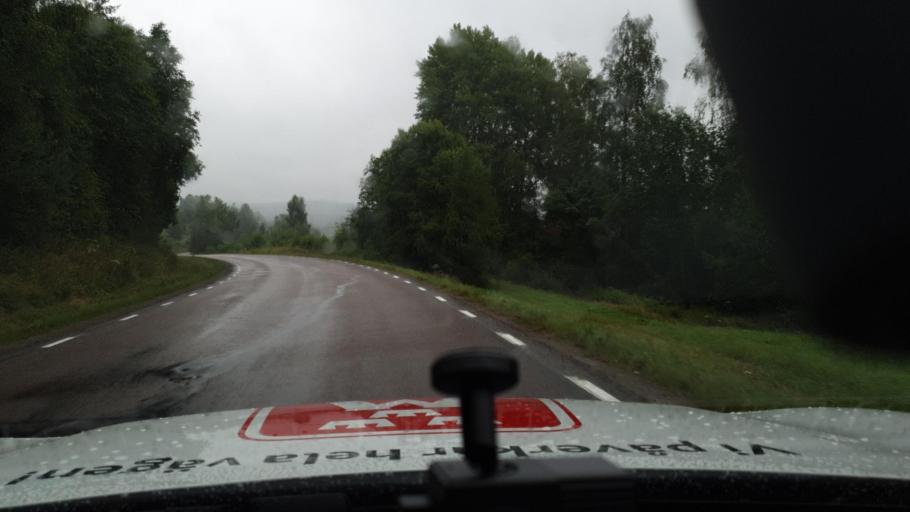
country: SE
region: Vaermland
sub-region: Eda Kommun
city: Amotfors
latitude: 59.8761
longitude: 12.5093
